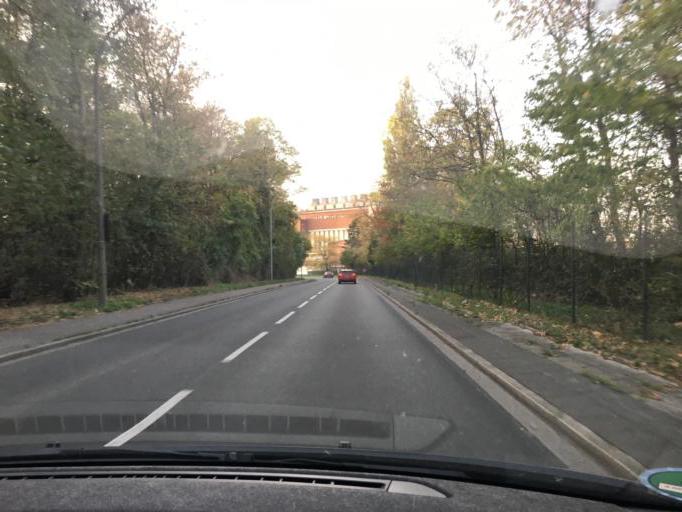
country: DE
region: North Rhine-Westphalia
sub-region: Regierungsbezirk Koln
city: Hurth
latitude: 50.8626
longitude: 6.8294
